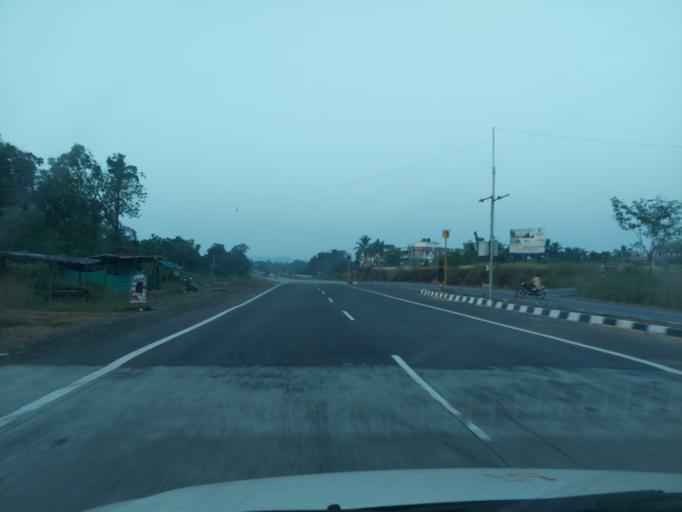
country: IN
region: Maharashtra
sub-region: Sindhudurg
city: Kudal
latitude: 16.0952
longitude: 73.7062
